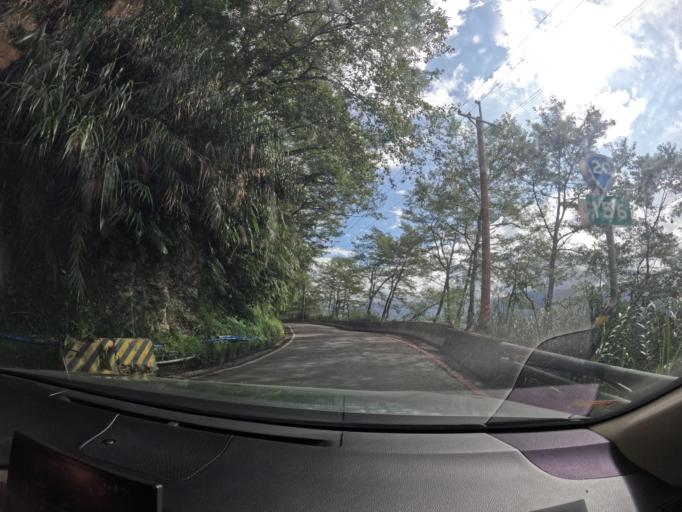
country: TW
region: Taiwan
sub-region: Taitung
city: Taitung
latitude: 23.2324
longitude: 121.0072
